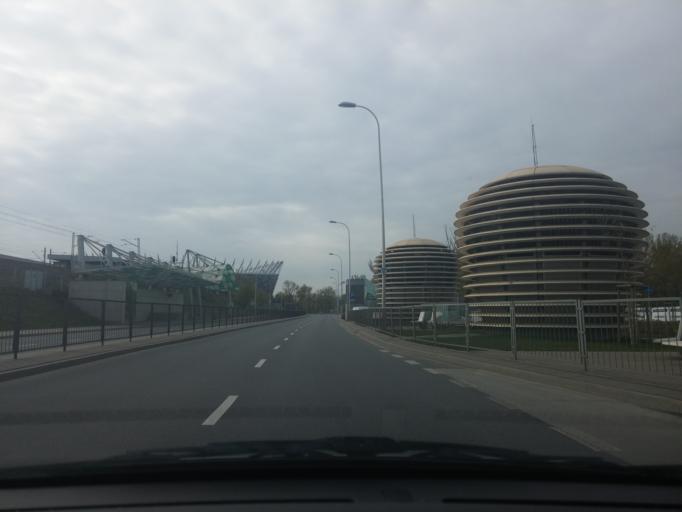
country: PL
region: Masovian Voivodeship
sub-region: Warszawa
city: Praga Polnoc
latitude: 52.2472
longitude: 21.0431
